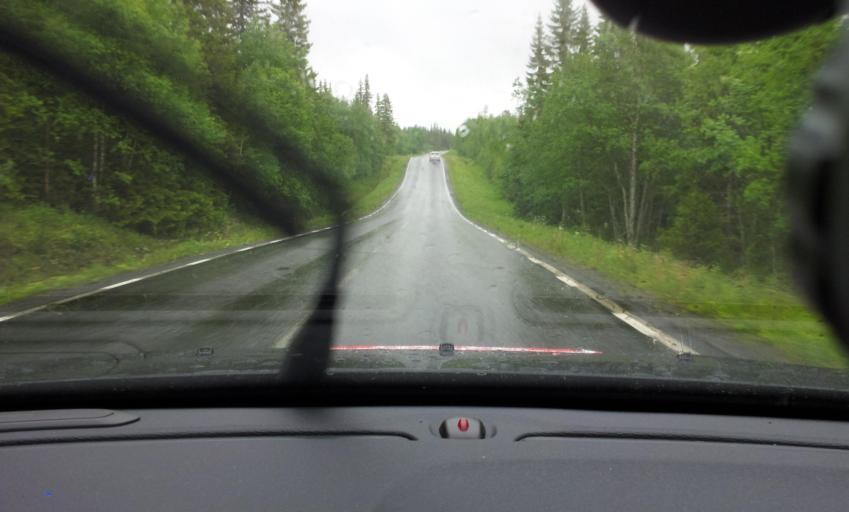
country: SE
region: Jaemtland
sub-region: Are Kommun
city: Are
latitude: 63.3150
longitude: 13.1454
